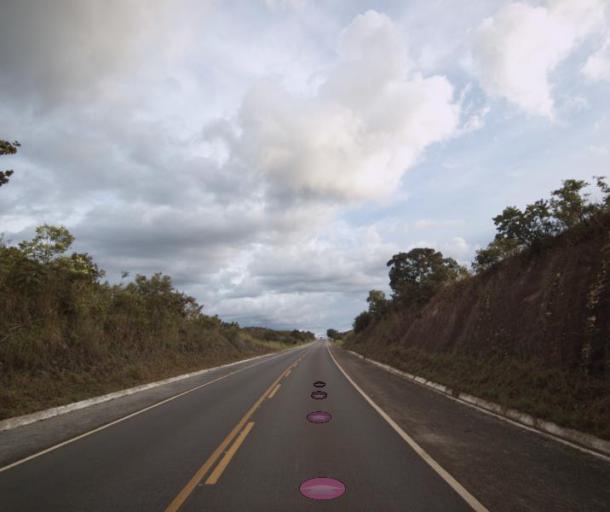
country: BR
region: Goias
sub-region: Barro Alto
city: Barro Alto
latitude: -14.8881
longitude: -48.6408
